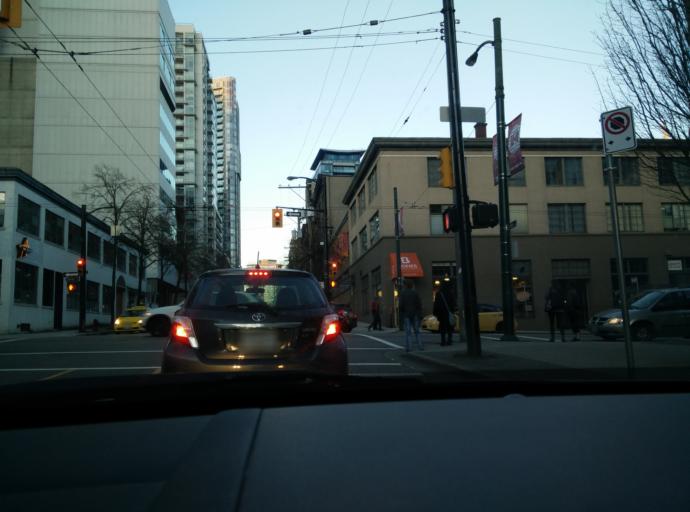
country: CA
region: British Columbia
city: West End
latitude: 49.2770
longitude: -123.1169
